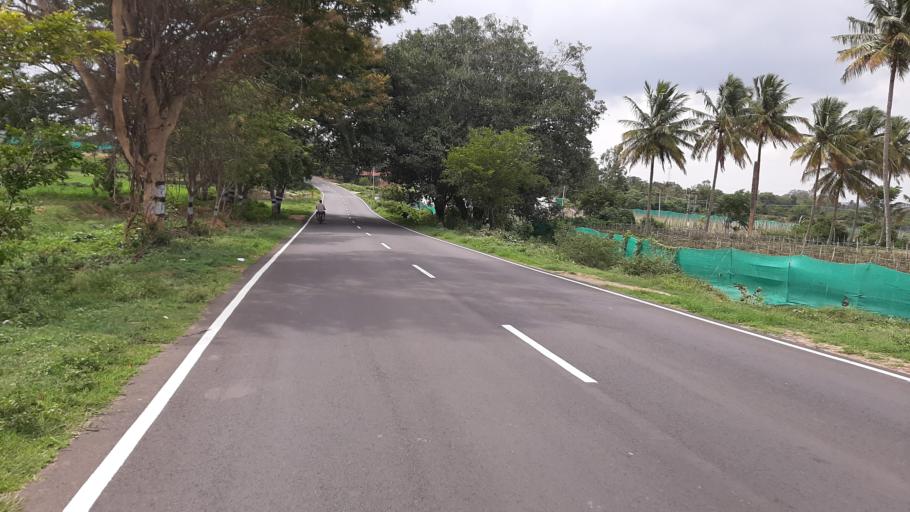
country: IN
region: Tamil Nadu
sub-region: Krishnagiri
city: Denkanikota
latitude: 12.5358
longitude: 77.7738
